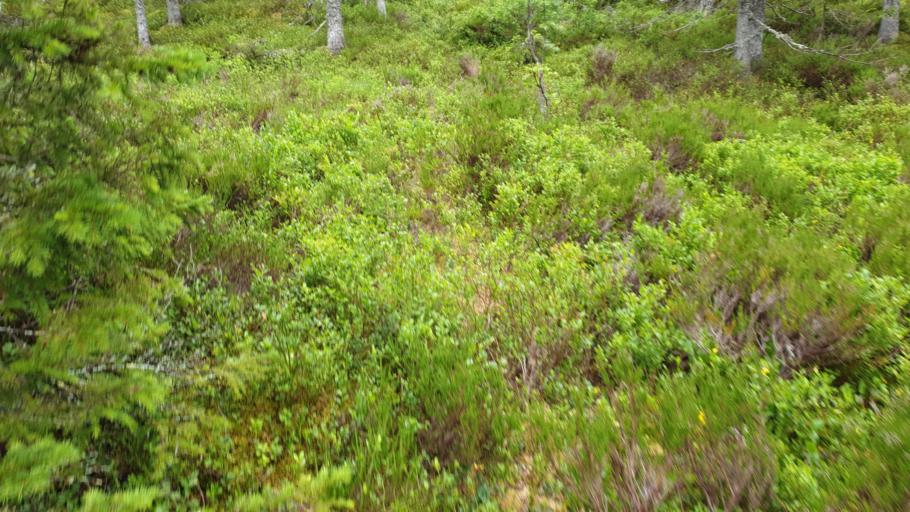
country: SE
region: Gaevleborg
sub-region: Hudiksvalls Kommun
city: Sorforsa
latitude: 61.6451
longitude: 16.7651
